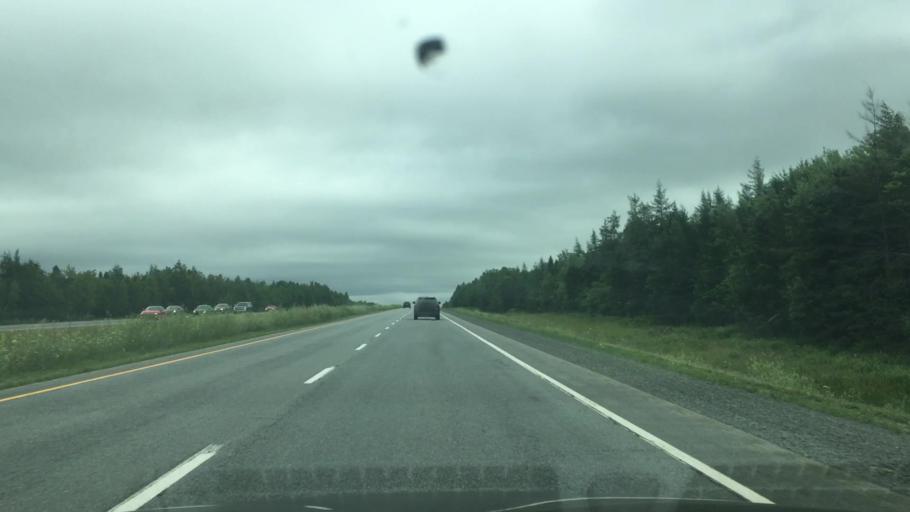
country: CA
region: Nova Scotia
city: Cole Harbour
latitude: 44.9999
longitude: -63.4880
